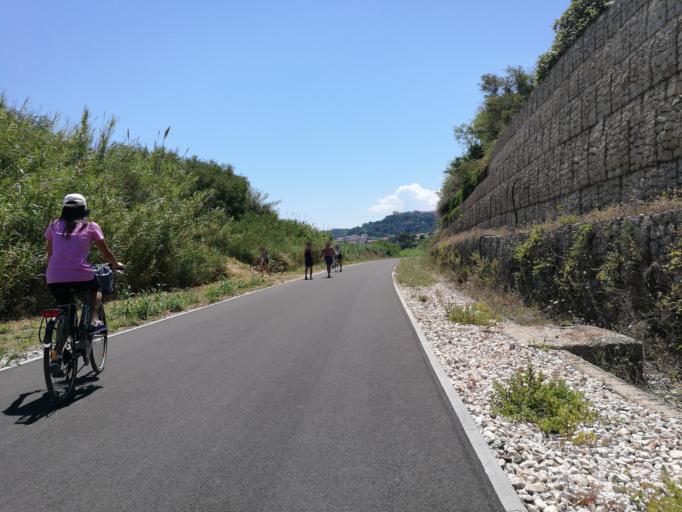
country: IT
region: Abruzzo
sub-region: Provincia di Chieti
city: Marina di San Vito
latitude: 42.3168
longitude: 14.4364
